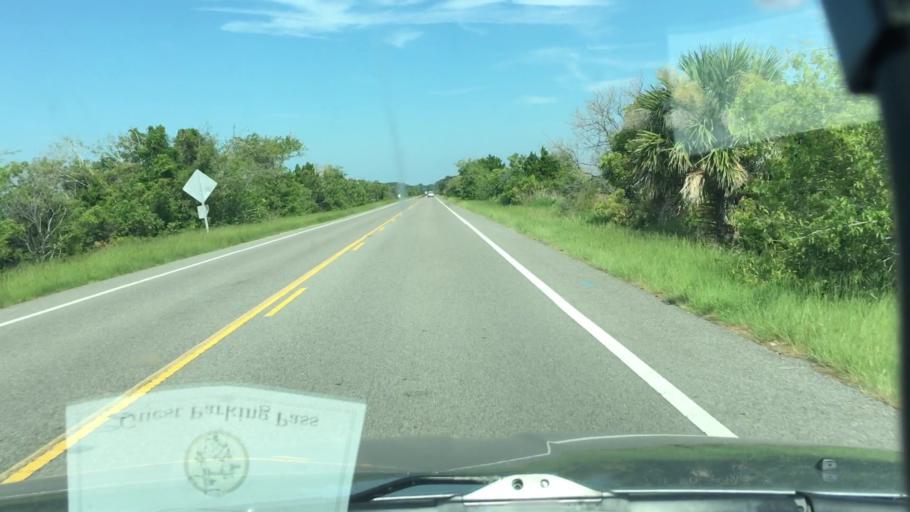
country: US
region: South Carolina
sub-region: Beaufort County
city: Beaufort
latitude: 32.4067
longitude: -80.4599
